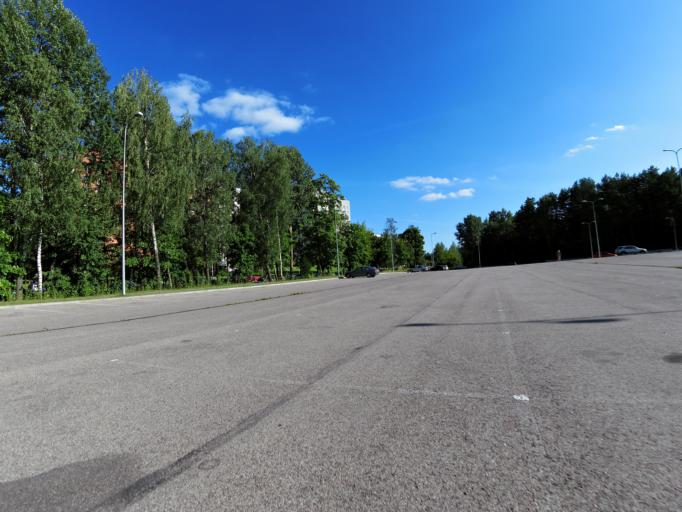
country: LT
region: Vilnius County
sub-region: Vilnius
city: Fabijoniskes
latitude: 54.7323
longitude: 25.2597
